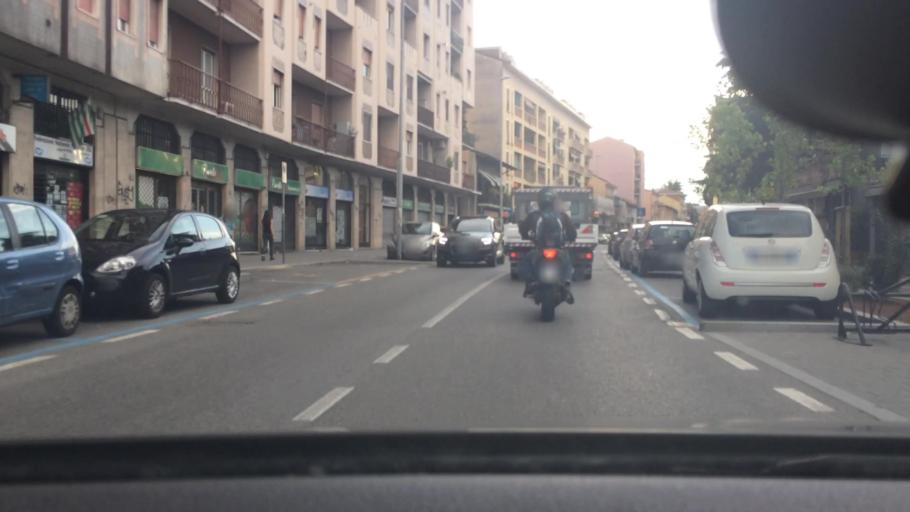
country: IT
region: Lombardy
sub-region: Citta metropolitana di Milano
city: Pero
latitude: 45.5087
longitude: 9.0905
